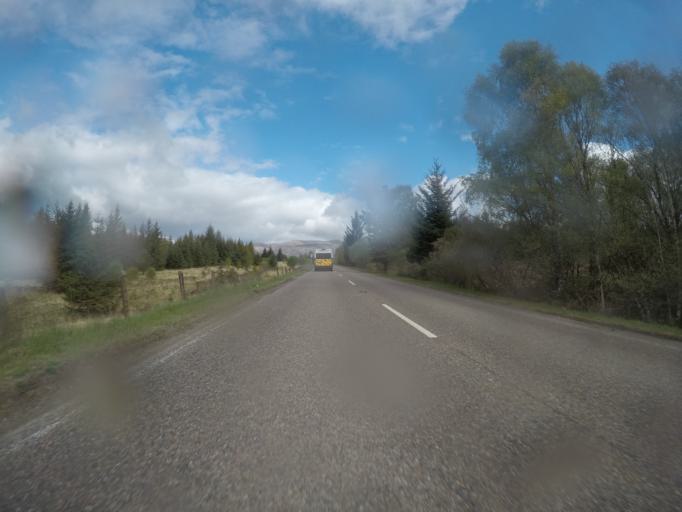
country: GB
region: Scotland
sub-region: Highland
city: Spean Bridge
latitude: 56.9035
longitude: -4.9445
